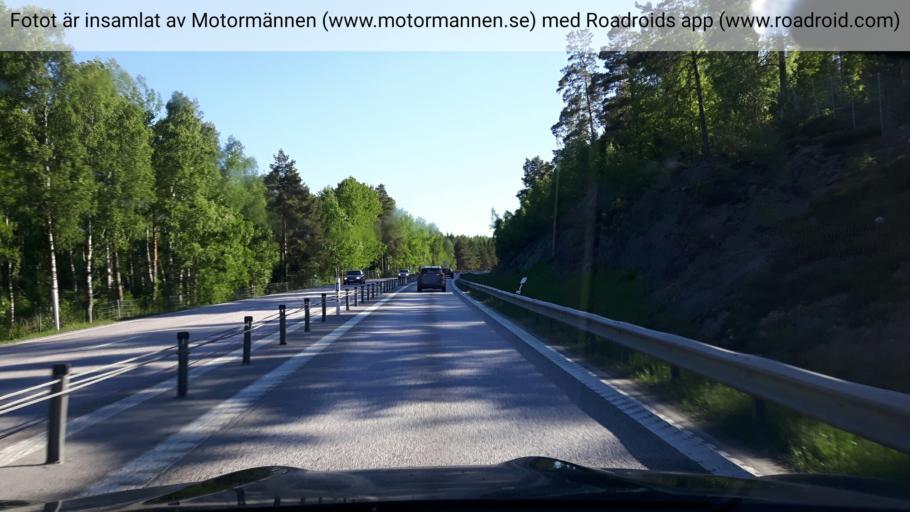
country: SE
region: Stockholm
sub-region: Vallentuna Kommun
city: Vallentuna
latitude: 59.5276
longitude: 18.1894
